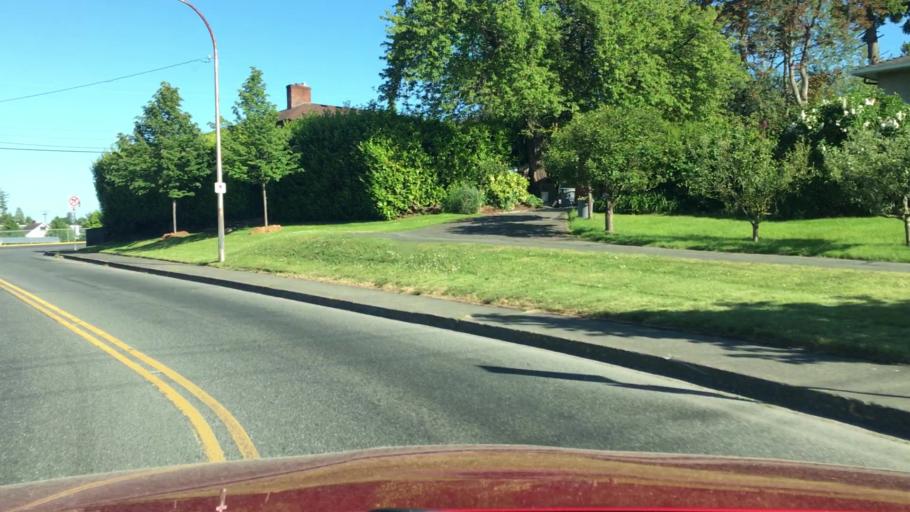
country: CA
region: British Columbia
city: Victoria
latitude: 48.4397
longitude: -123.4027
